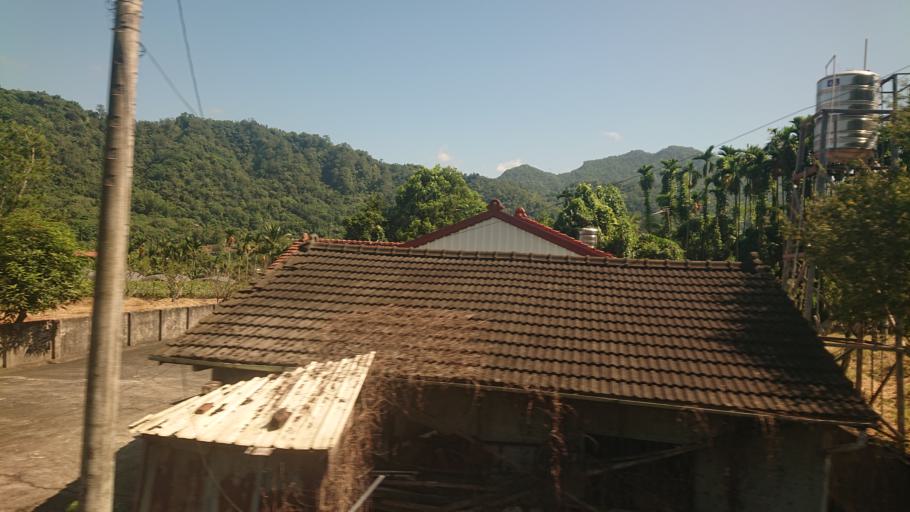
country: TW
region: Taiwan
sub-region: Nantou
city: Puli
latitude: 24.0591
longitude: 120.9372
